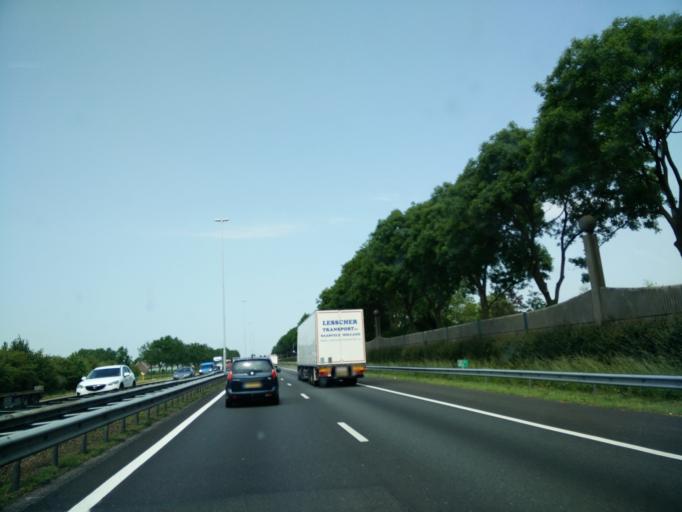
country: NL
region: Utrecht
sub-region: Gemeente Lopik
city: Lopik
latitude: 51.9200
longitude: 4.9892
